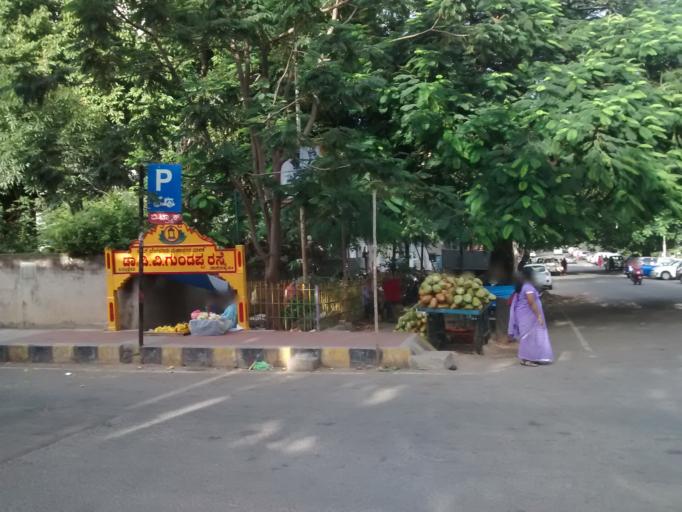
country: IN
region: Karnataka
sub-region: Bangalore Urban
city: Bangalore
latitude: 12.9422
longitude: 77.5711
